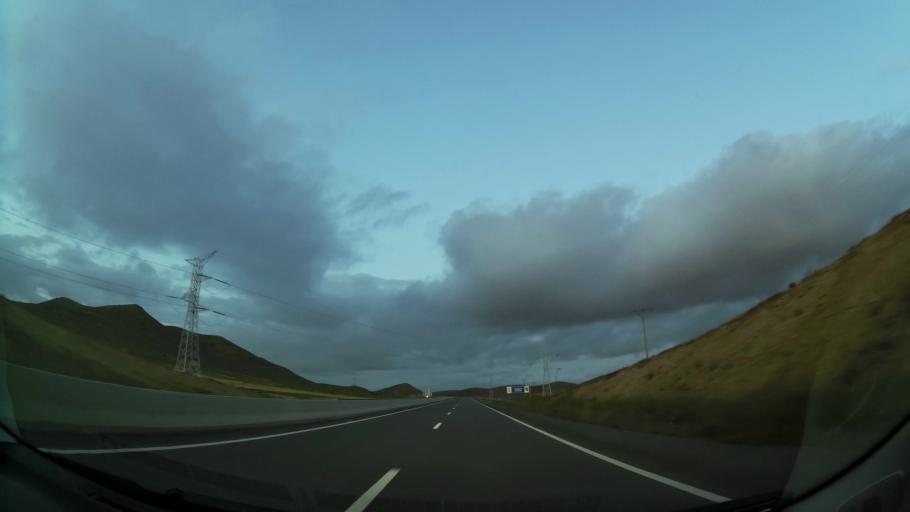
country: MA
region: Oriental
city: El Aioun
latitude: 34.6146
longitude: -2.4313
